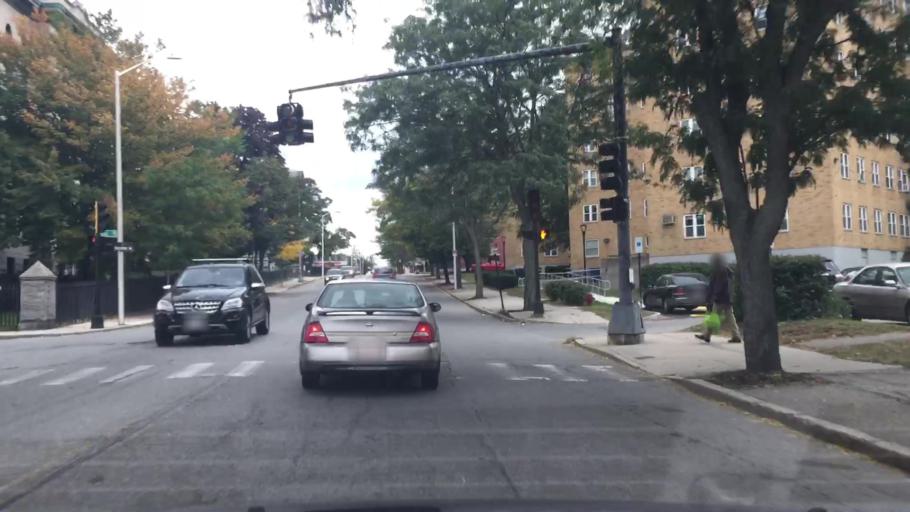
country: US
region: Massachusetts
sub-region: Middlesex County
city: Lowell
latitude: 42.6392
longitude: -71.3089
